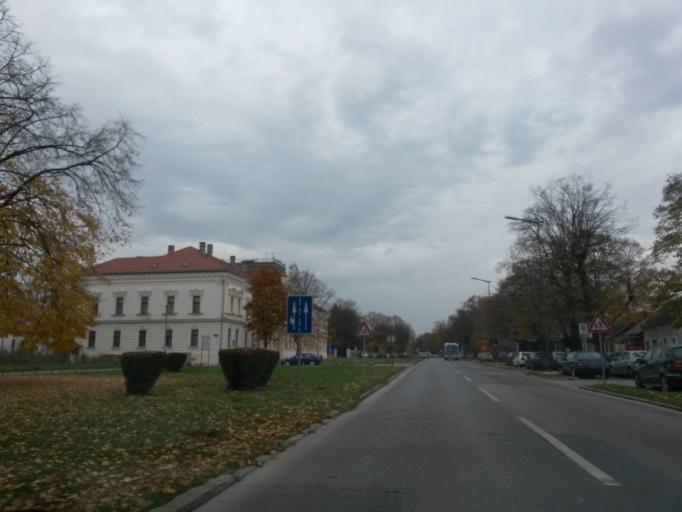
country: HR
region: Vukovarsko-Srijemska
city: Vukovar
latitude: 45.3572
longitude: 18.9962
